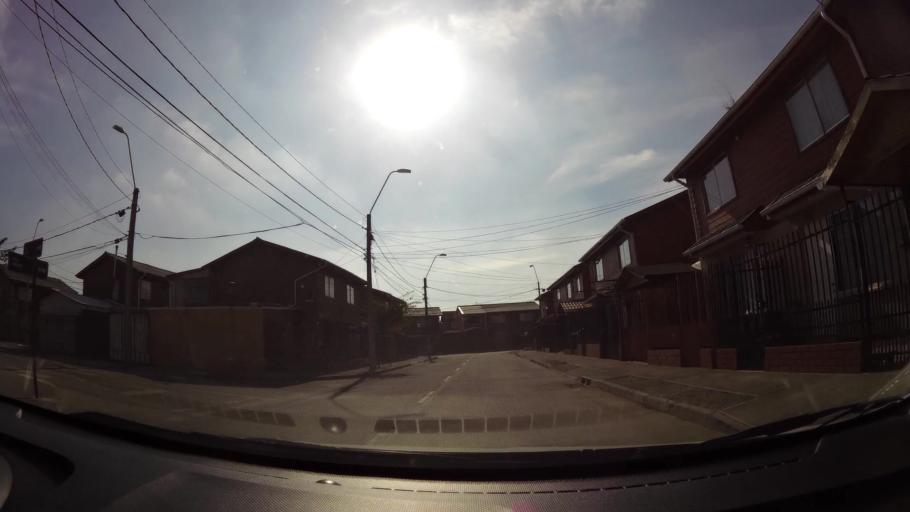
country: CL
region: Biobio
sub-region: Provincia de Concepcion
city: Talcahuano
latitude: -36.7944
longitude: -73.1159
